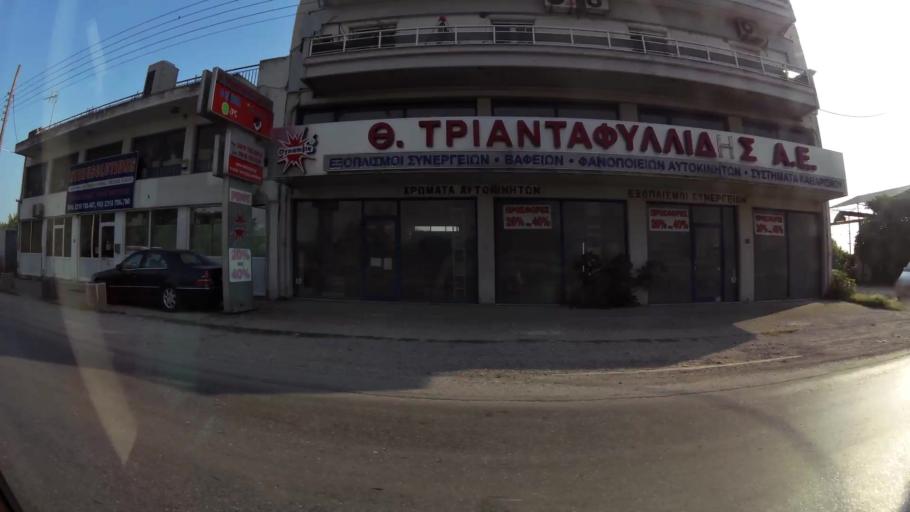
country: GR
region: Central Macedonia
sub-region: Nomos Thessalonikis
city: Diavata
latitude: 40.6824
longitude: 22.8621
